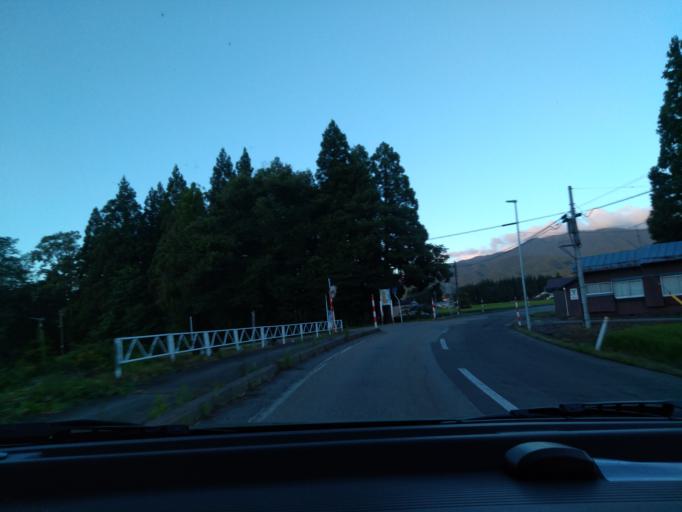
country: JP
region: Akita
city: Kakunodatemachi
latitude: 39.5830
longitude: 140.5892
